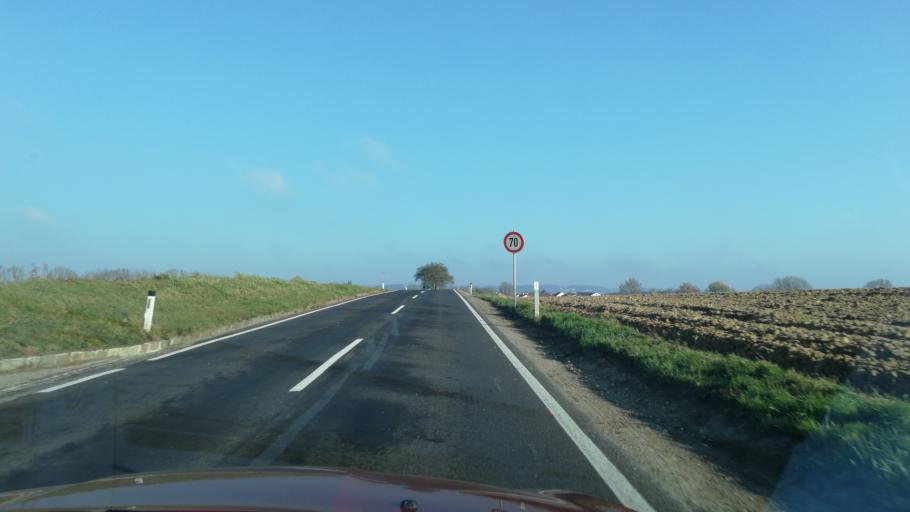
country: AT
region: Upper Austria
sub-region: Wels-Land
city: Buchkirchen
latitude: 48.2068
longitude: 14.0356
